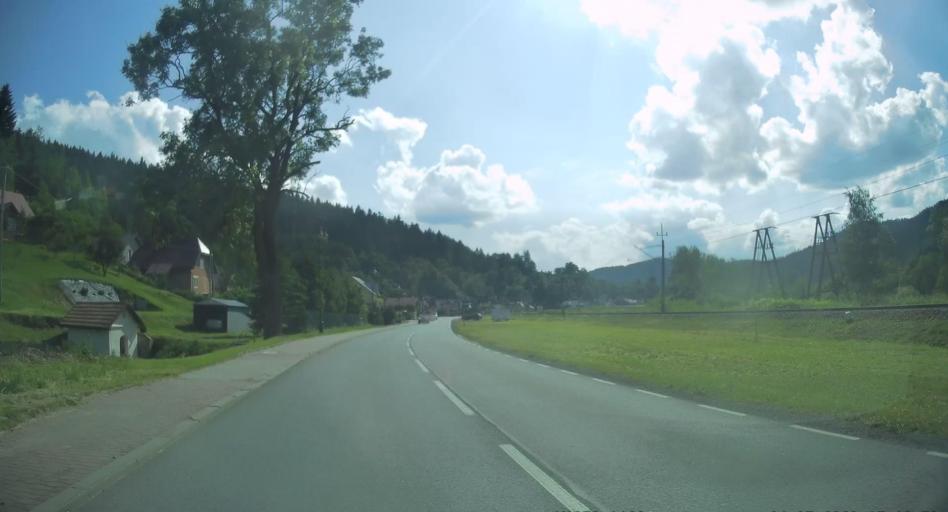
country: PL
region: Lesser Poland Voivodeship
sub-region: Powiat nowosadecki
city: Muszyna
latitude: 49.3602
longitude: 20.9149
